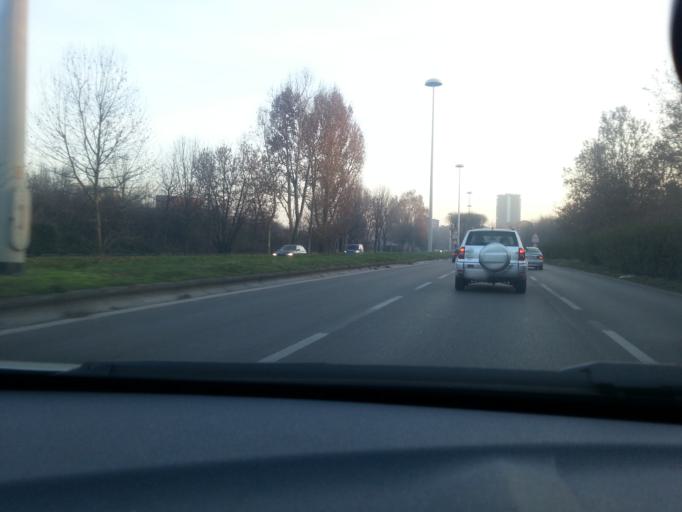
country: IT
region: Lombardy
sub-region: Citta metropolitana di Milano
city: Bresso
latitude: 45.5113
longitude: 9.1801
